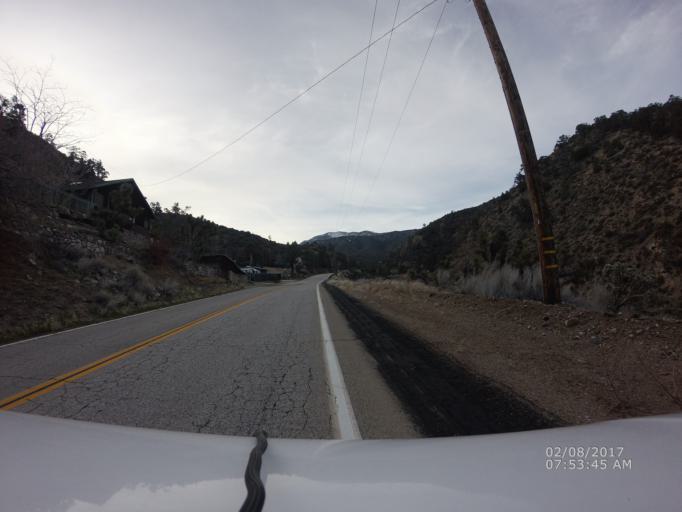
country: US
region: California
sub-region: San Bernardino County
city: Pinon Hills
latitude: 34.4288
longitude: -117.7665
